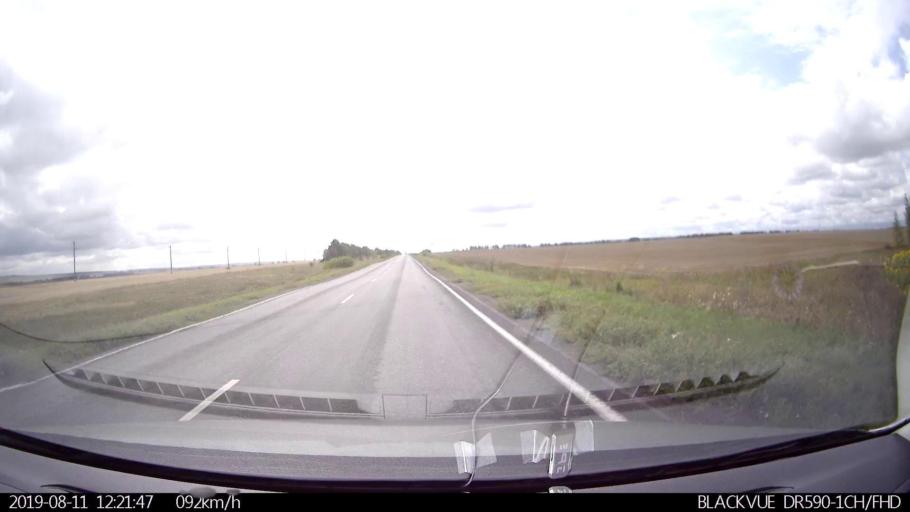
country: RU
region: Ulyanovsk
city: Ignatovka
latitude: 53.9167
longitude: 47.9567
